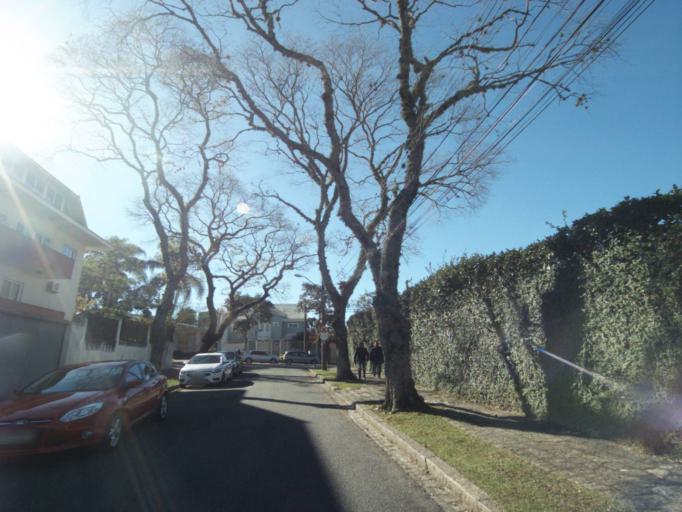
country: BR
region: Parana
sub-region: Curitiba
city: Curitiba
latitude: -25.4188
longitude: -49.2505
